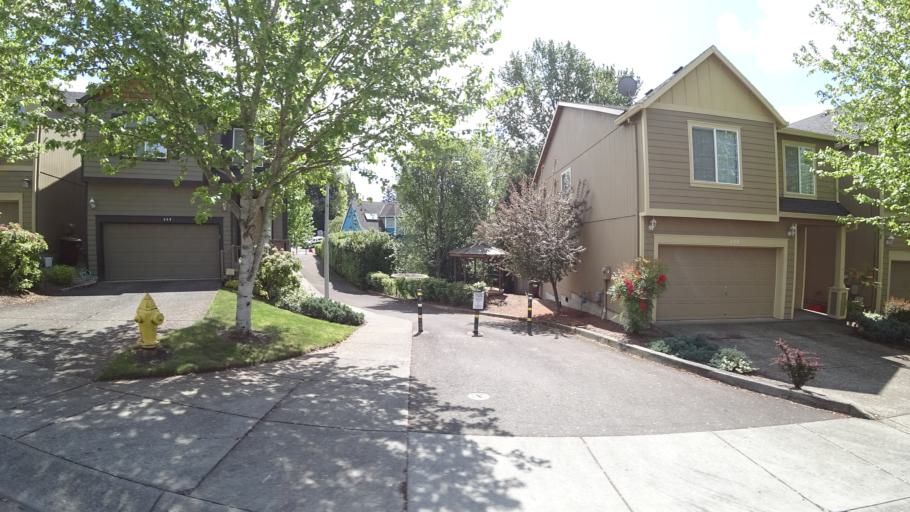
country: US
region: Oregon
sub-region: Washington County
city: Hillsboro
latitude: 45.5145
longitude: -122.9817
